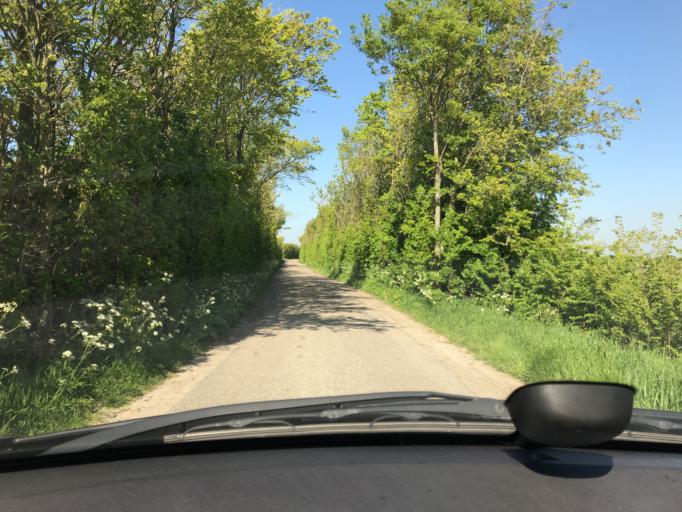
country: NL
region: Zeeland
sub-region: Gemeente Vlissingen
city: Vlissingen
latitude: 51.5136
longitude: 3.4767
